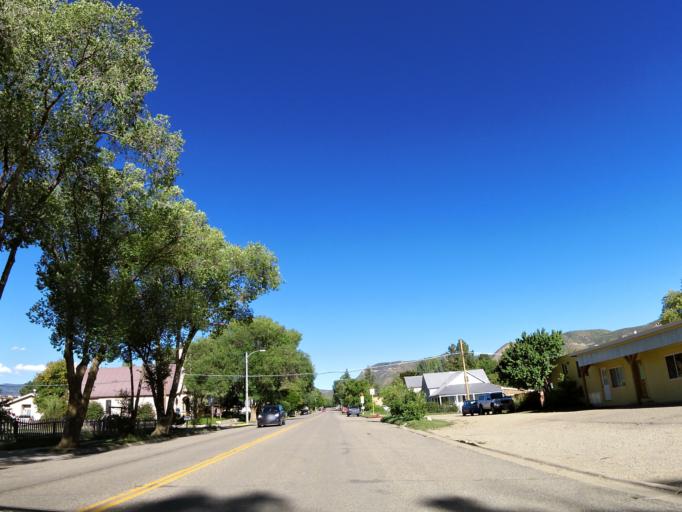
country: US
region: Colorado
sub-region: Montezuma County
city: Mancos
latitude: 37.3450
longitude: -108.2956
